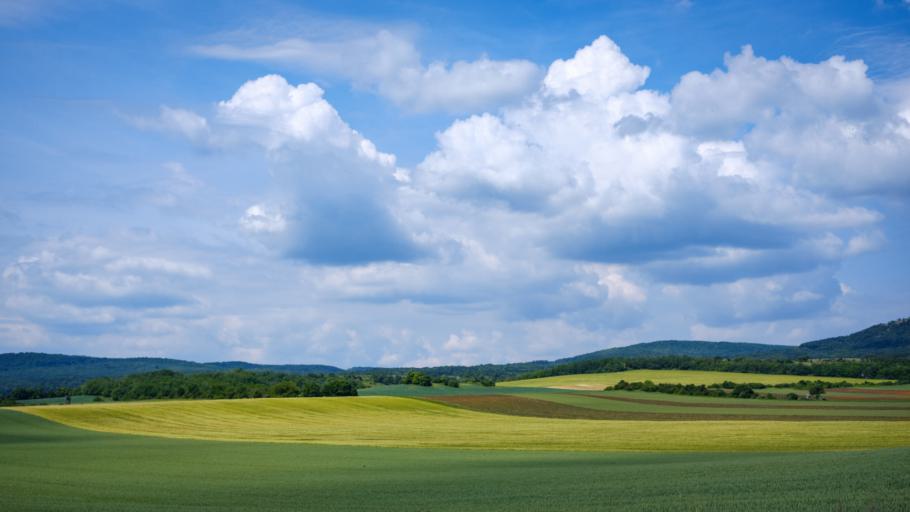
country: HU
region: Fejer
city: Szarliget
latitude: 47.4663
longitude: 18.5096
